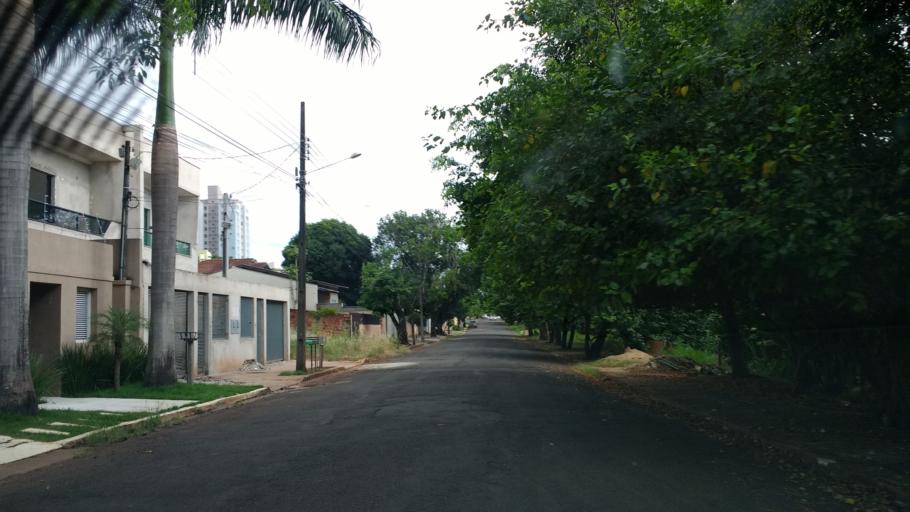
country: BR
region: Parana
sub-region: Londrina
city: Londrina
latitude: -23.3078
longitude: -51.1812
